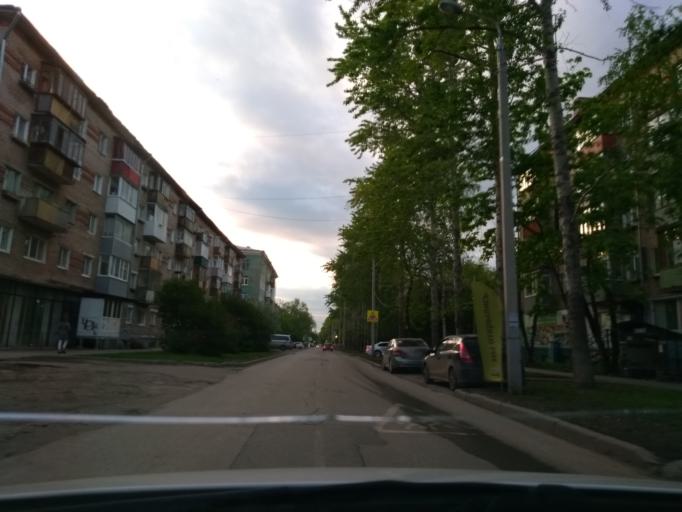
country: RU
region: Perm
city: Perm
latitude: 57.9968
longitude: 56.2579
